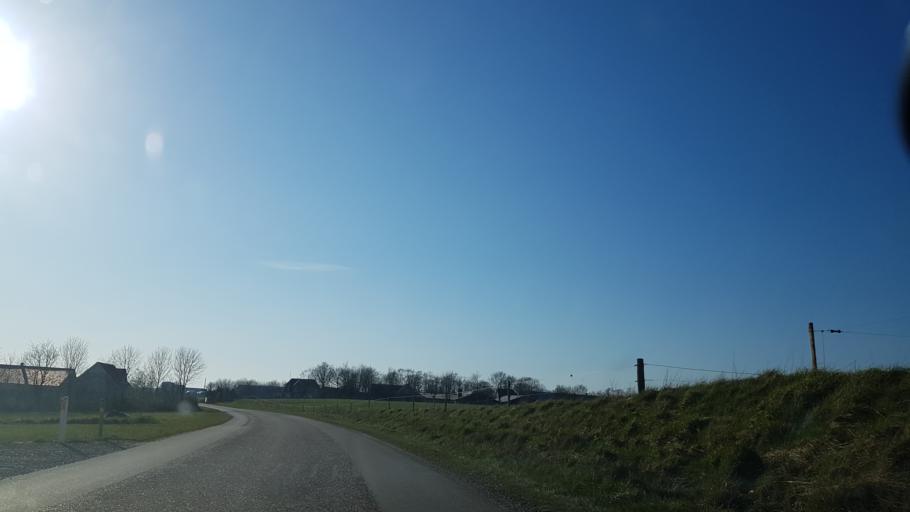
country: DK
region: South Denmark
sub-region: Vejen Kommune
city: Rodding
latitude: 55.3848
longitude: 8.9853
